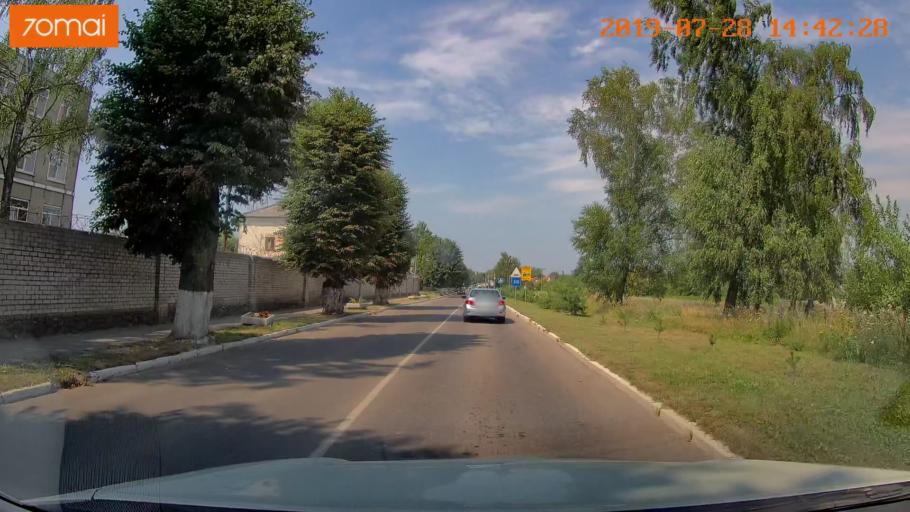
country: RU
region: Kaliningrad
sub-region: Gorod Kaliningrad
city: Yantarnyy
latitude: 54.8601
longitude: 19.9420
